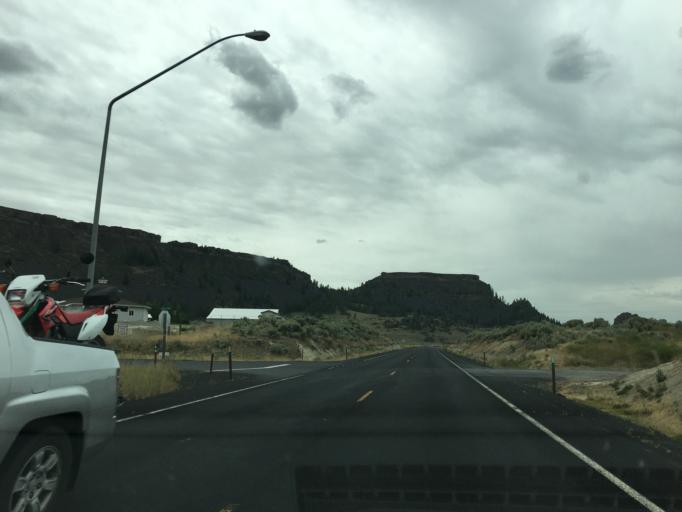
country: US
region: Washington
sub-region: Okanogan County
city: Coulee Dam
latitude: 47.8962
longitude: -119.0722
